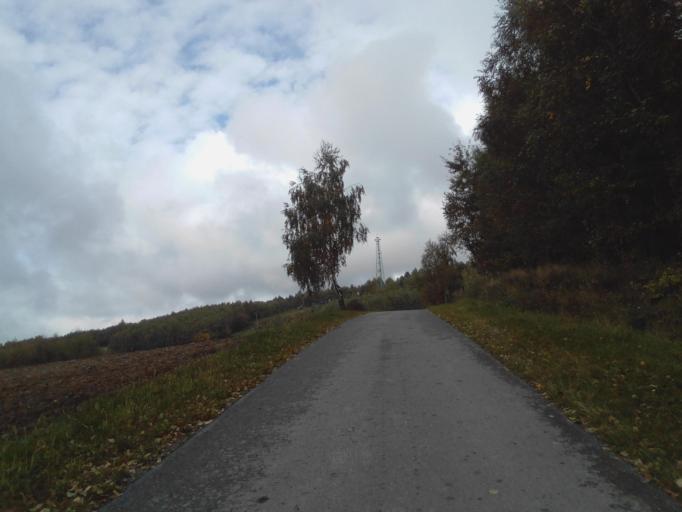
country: PL
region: Subcarpathian Voivodeship
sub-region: Powiat strzyzowski
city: Gwoznica Gorna
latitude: 49.8355
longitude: 22.0190
